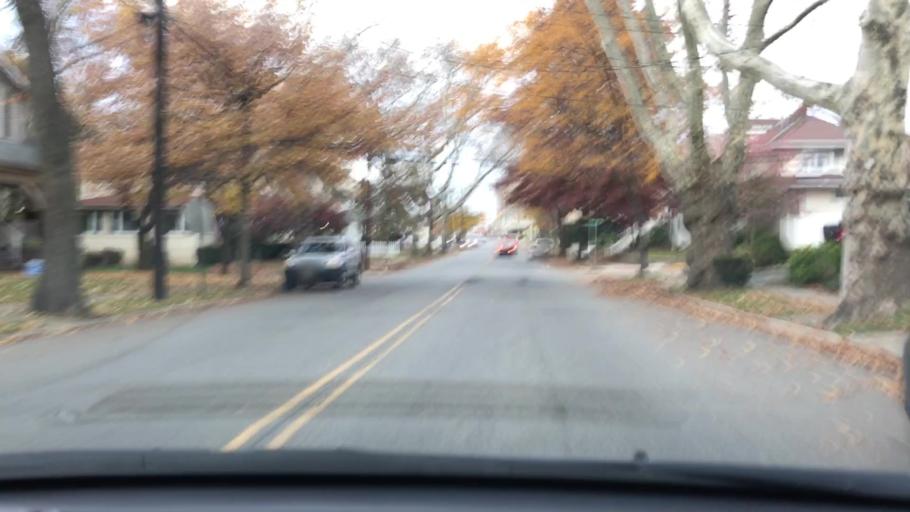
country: US
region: New Jersey
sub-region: Bergen County
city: Bogota
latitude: 40.8738
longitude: -74.0264
